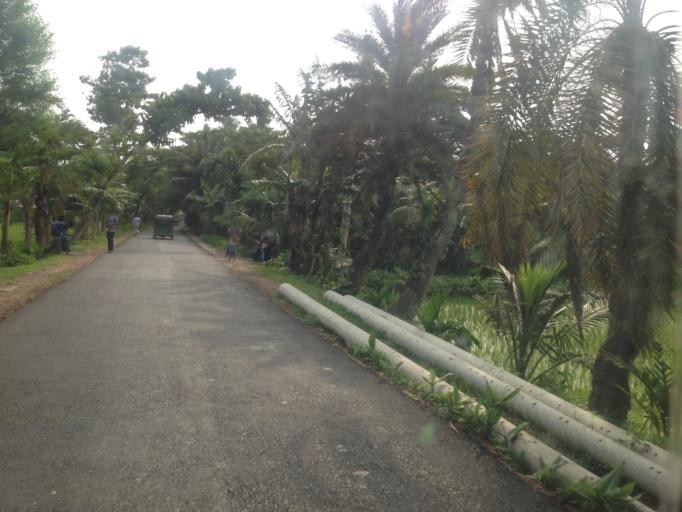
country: BD
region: Chittagong
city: Raipur
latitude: 23.0347
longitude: 90.7190
